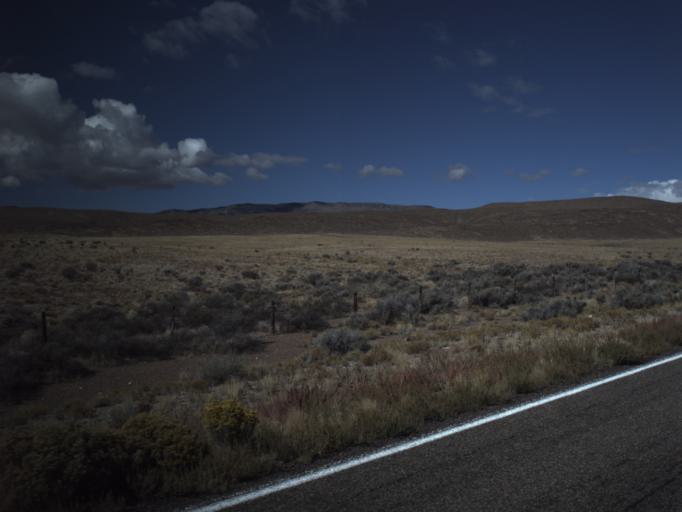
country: US
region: Utah
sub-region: Beaver County
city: Milford
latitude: 38.5929
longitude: -113.8222
